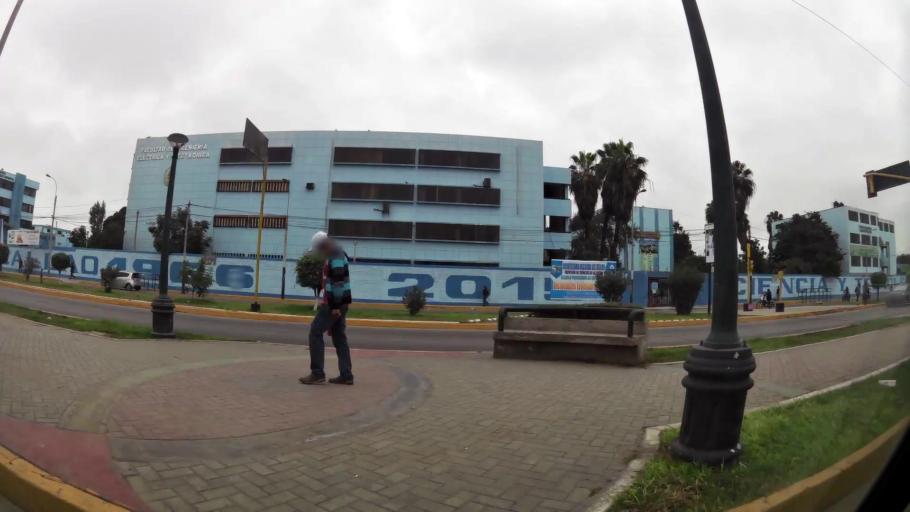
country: PE
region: Callao
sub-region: Callao
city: Callao
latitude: -12.0618
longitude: -77.1167
